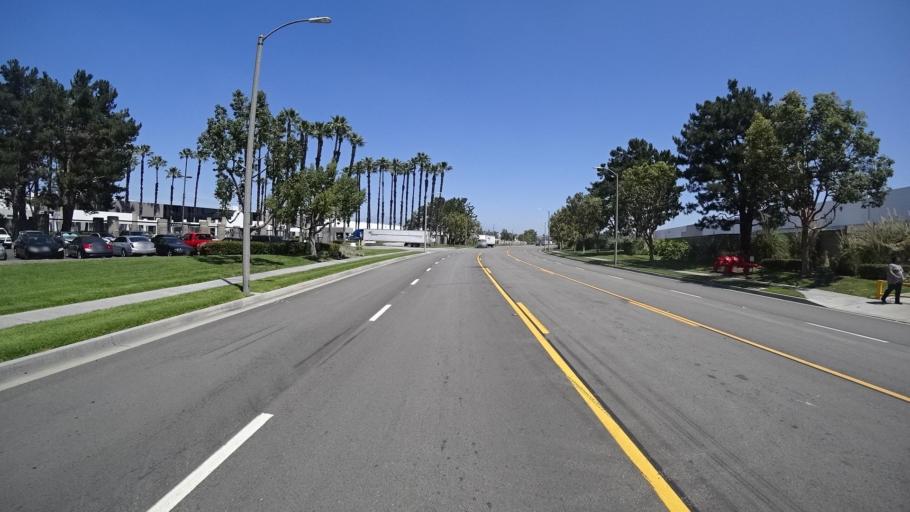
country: US
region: California
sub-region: Los Angeles County
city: Walnut
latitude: 34.0013
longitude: -117.8650
